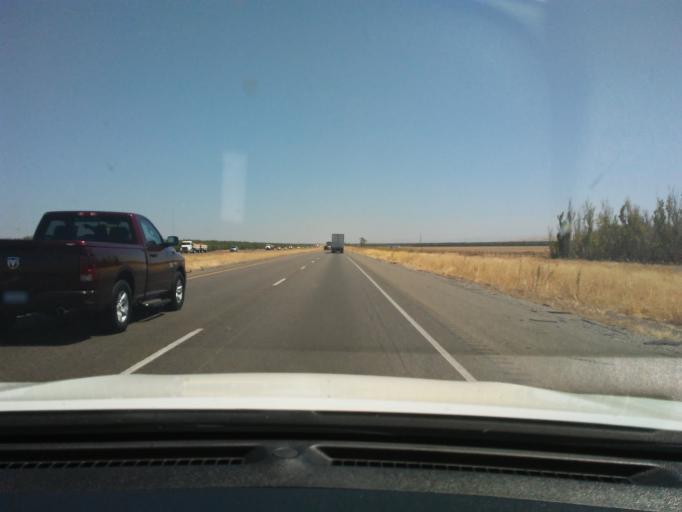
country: US
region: California
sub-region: Merced County
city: South Dos Palos
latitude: 36.8010
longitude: -120.7403
